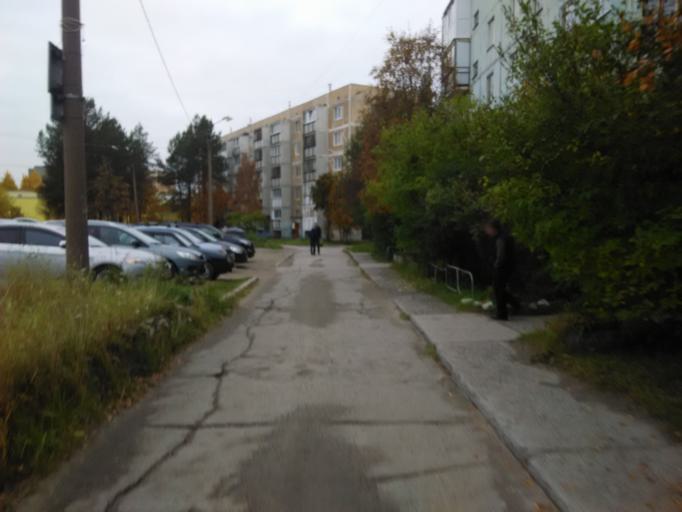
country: RU
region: Murmansk
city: Polyarnyye Zori
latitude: 67.3719
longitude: 32.5029
